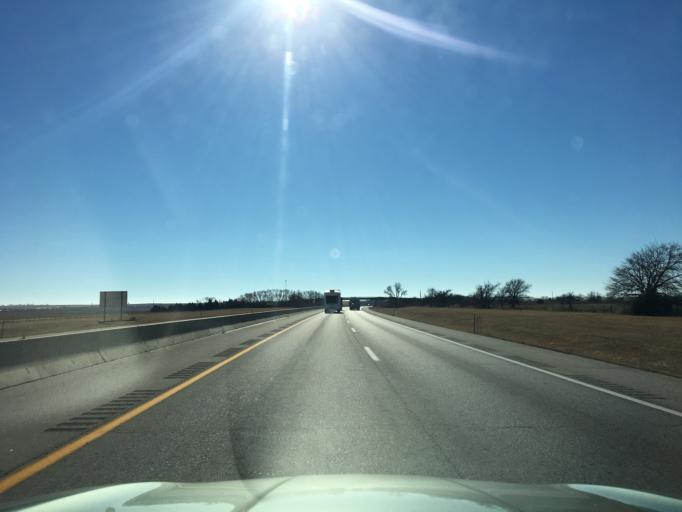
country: US
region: Oklahoma
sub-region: Kay County
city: Blackwell
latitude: 37.0177
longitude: -97.3382
